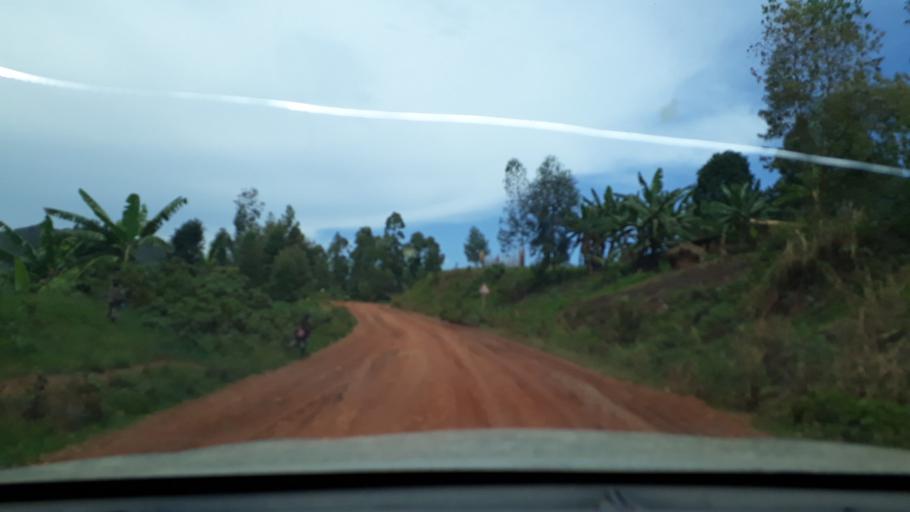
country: CD
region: Eastern Province
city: Bunia
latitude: 1.7289
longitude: 30.3223
